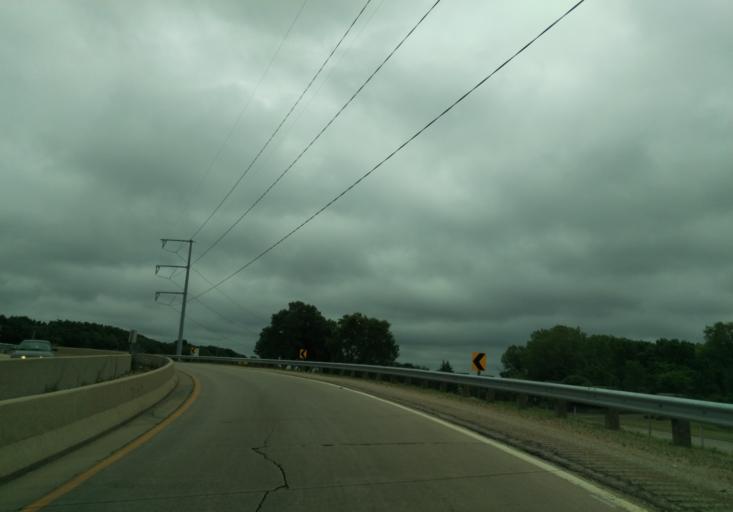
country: US
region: Wisconsin
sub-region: Dane County
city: Monona
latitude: 43.0425
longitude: -89.3689
